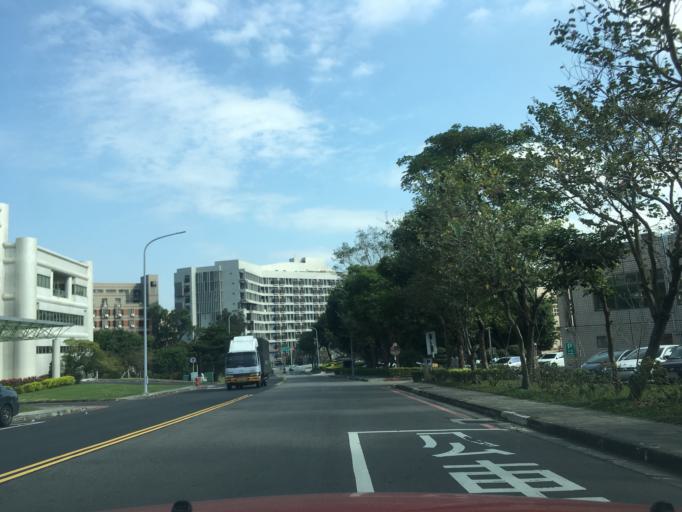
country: TW
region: Taiwan
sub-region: Hsinchu
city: Hsinchu
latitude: 24.7820
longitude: 120.9956
